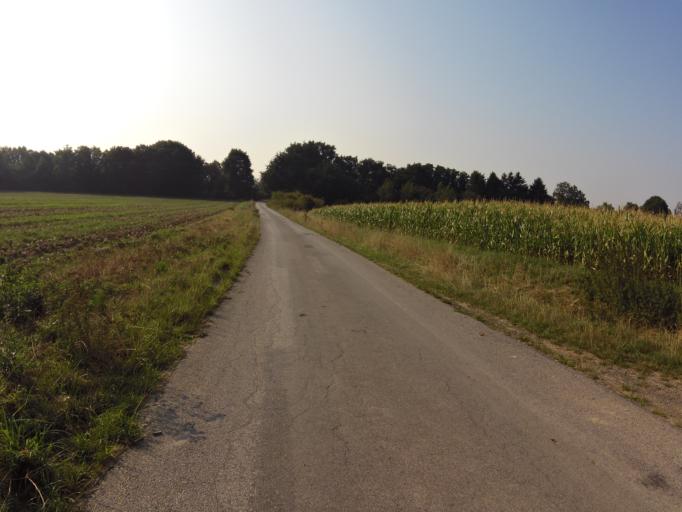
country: DE
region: North Rhine-Westphalia
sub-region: Regierungsbezirk Munster
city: Billerbeck
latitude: 51.9763
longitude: 7.3235
